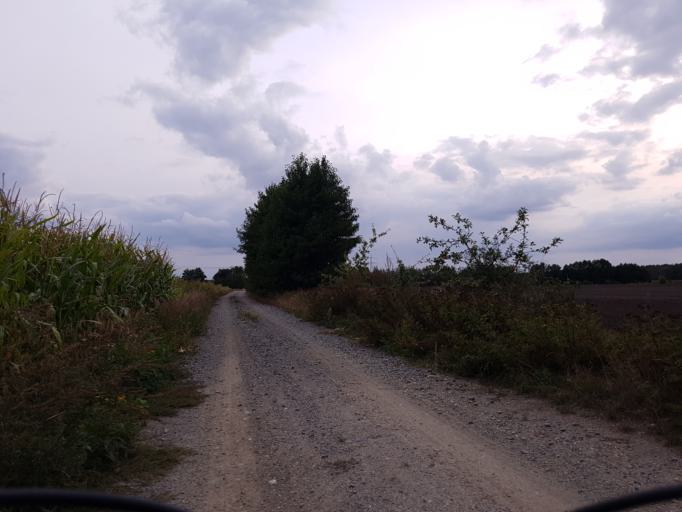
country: DE
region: Brandenburg
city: Trobitz
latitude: 51.5481
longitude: 13.4461
